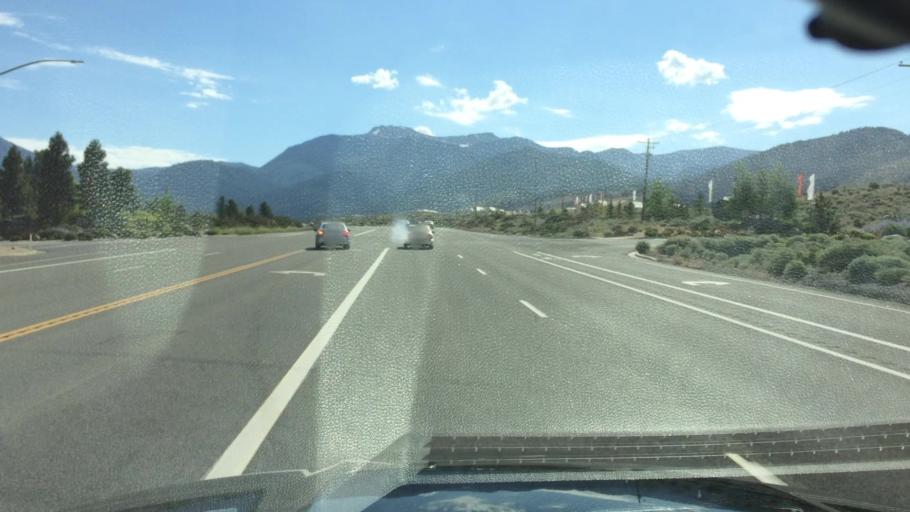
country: US
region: Nevada
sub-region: Washoe County
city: Reno
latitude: 39.3857
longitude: -119.8141
